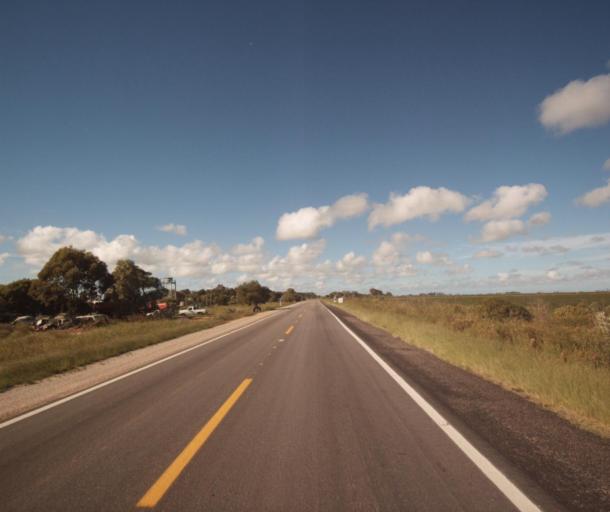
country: UY
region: Cerro Largo
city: Rio Branco
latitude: -33.0377
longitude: -52.8597
